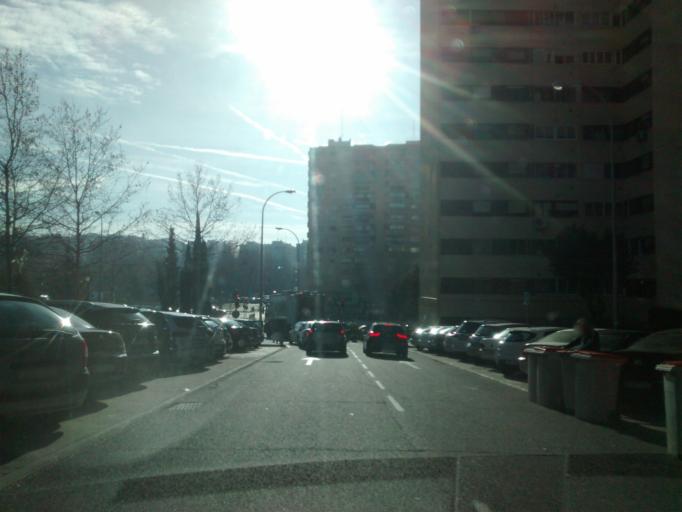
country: ES
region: Madrid
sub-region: Provincia de Madrid
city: Tetuan de las Victorias
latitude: 40.4811
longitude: -3.7137
